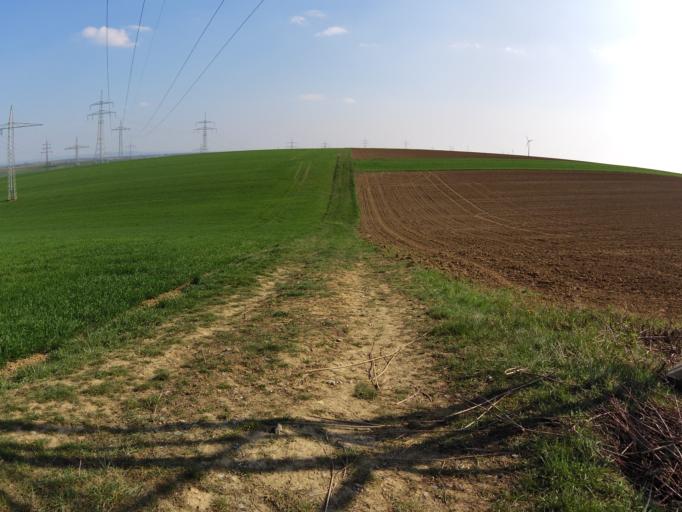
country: DE
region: Bavaria
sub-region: Regierungsbezirk Unterfranken
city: Theilheim
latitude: 49.7675
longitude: 10.0474
